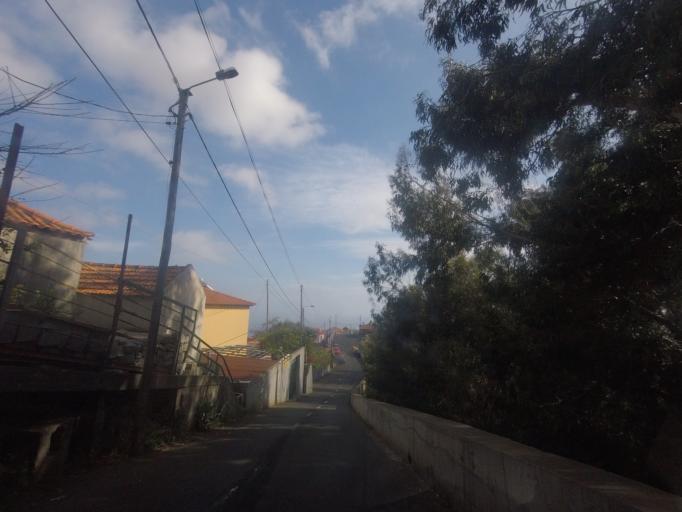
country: PT
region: Madeira
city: Camara de Lobos
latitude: 32.6748
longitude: -16.9540
